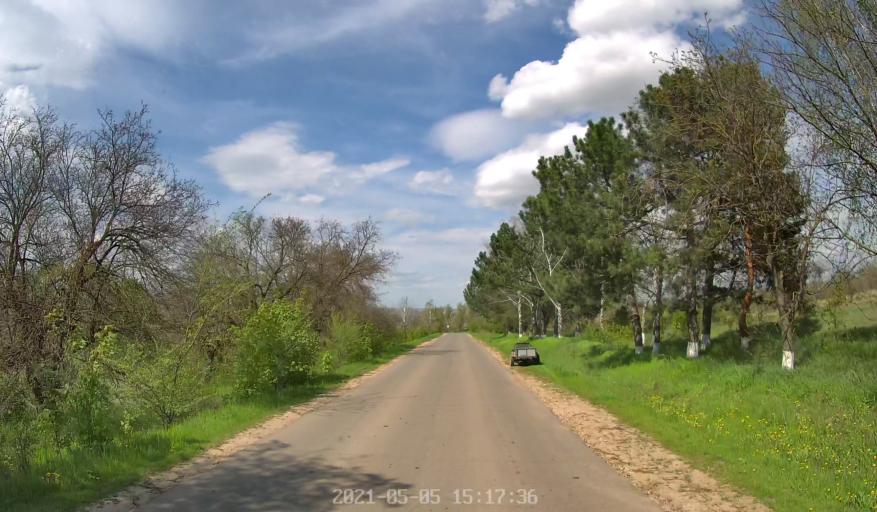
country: MD
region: Criuleni
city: Criuleni
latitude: 47.1132
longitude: 29.1942
